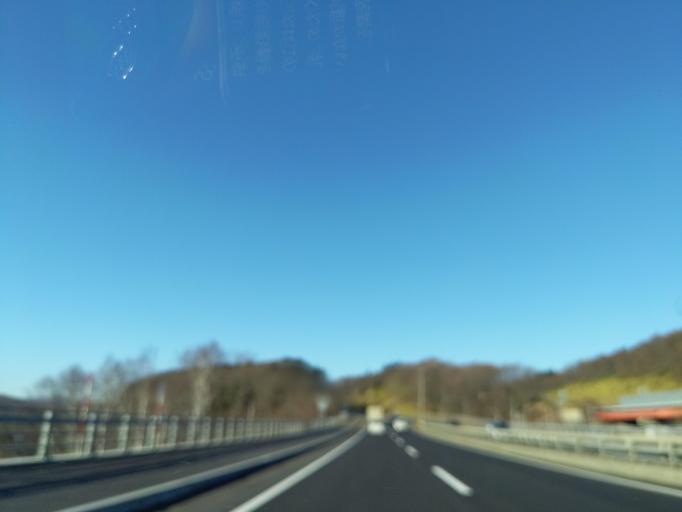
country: JP
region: Hokkaido
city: Kitahiroshima
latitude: 42.9228
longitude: 141.5409
